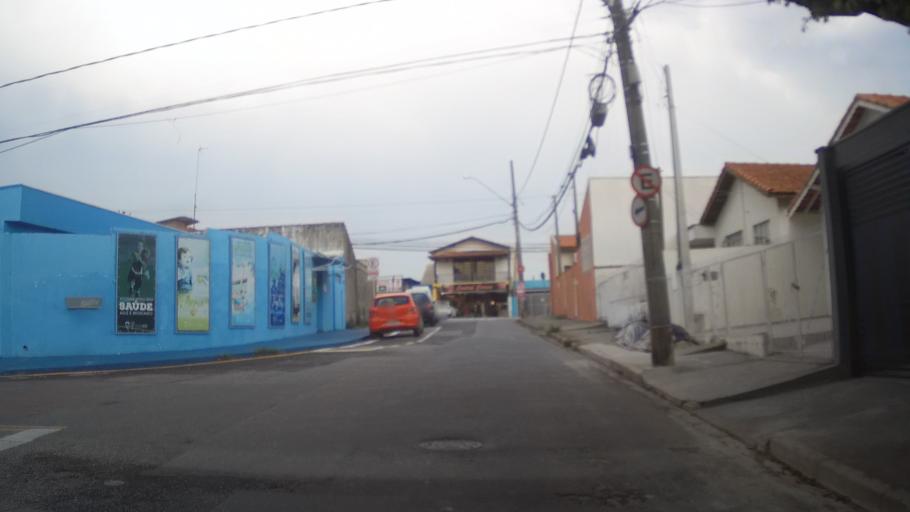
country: BR
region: Sao Paulo
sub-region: Jundiai
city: Jundiai
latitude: -23.1839
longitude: -46.9606
